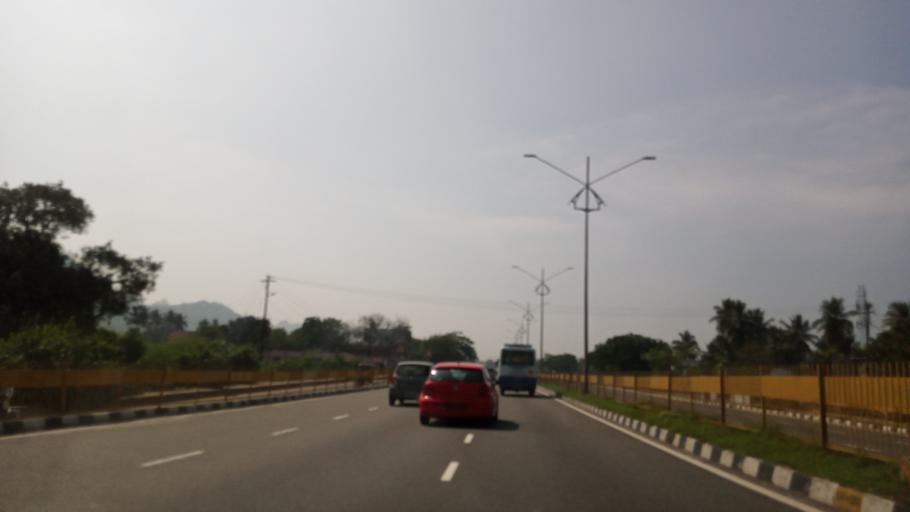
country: IN
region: Tamil Nadu
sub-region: Vellore
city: Katpadi
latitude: 12.9419
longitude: 79.1843
